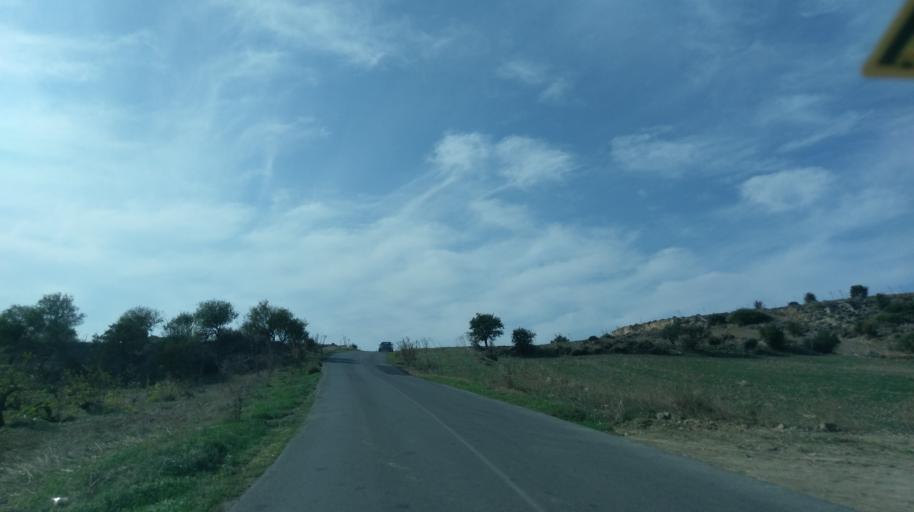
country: CY
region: Keryneia
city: Lapithos
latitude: 35.2826
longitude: 33.2321
